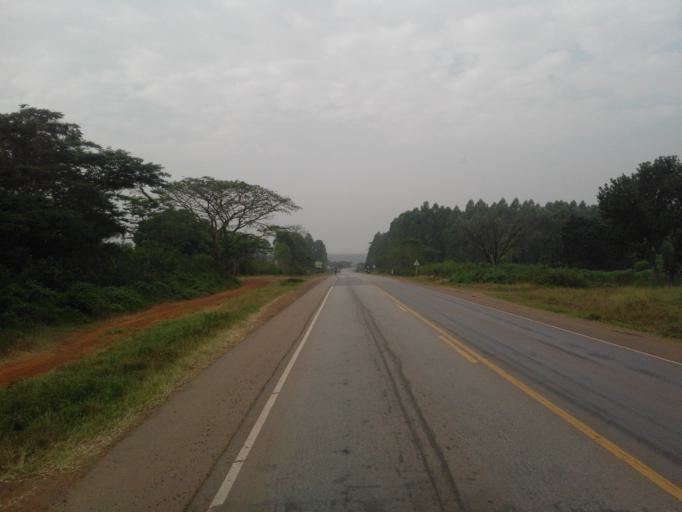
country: UG
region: Eastern Region
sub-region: Busia District
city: Busia
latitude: 0.5978
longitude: 34.0627
